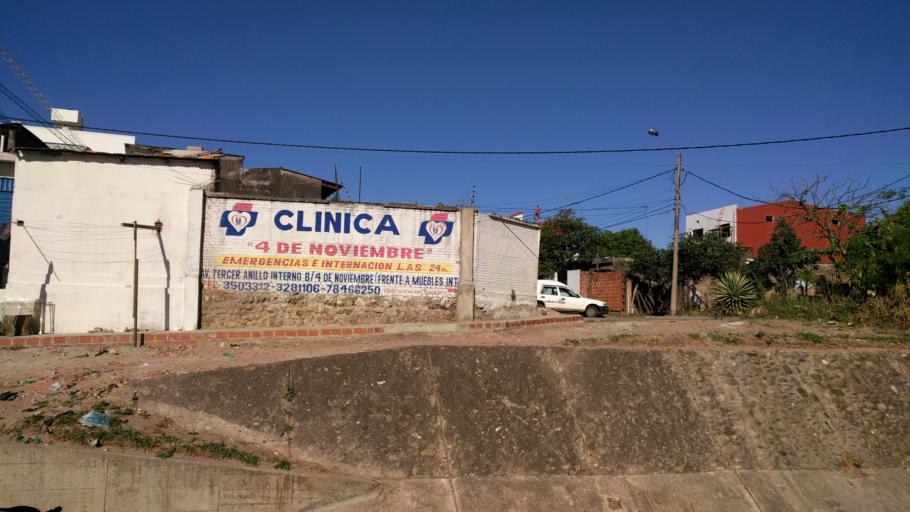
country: BO
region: Santa Cruz
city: Santa Cruz de la Sierra
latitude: -17.7779
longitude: -63.2052
